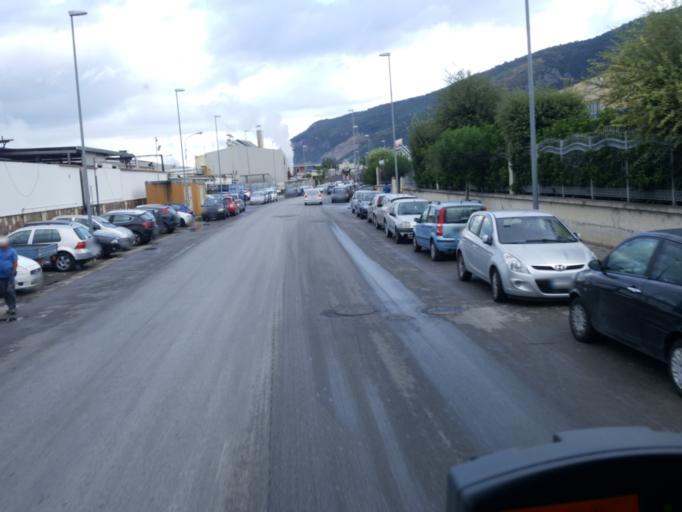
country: IT
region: Campania
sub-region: Provincia di Salerno
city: Sarno
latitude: 40.8204
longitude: 14.6007
